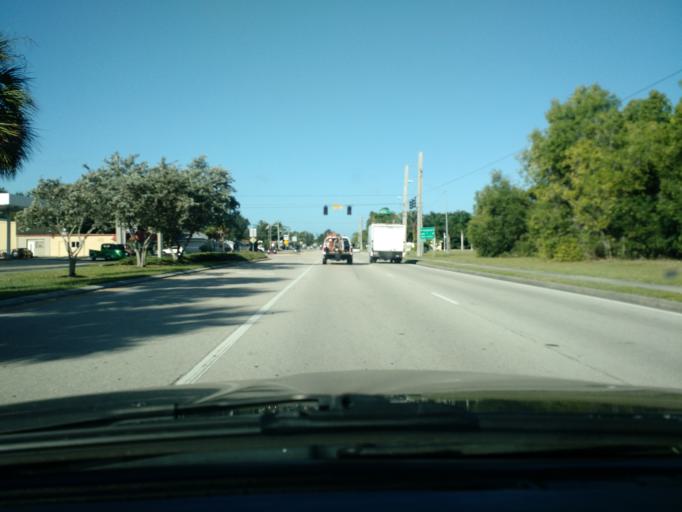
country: US
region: Florida
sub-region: Lee County
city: Bonita Springs
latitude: 26.3306
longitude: -81.8164
